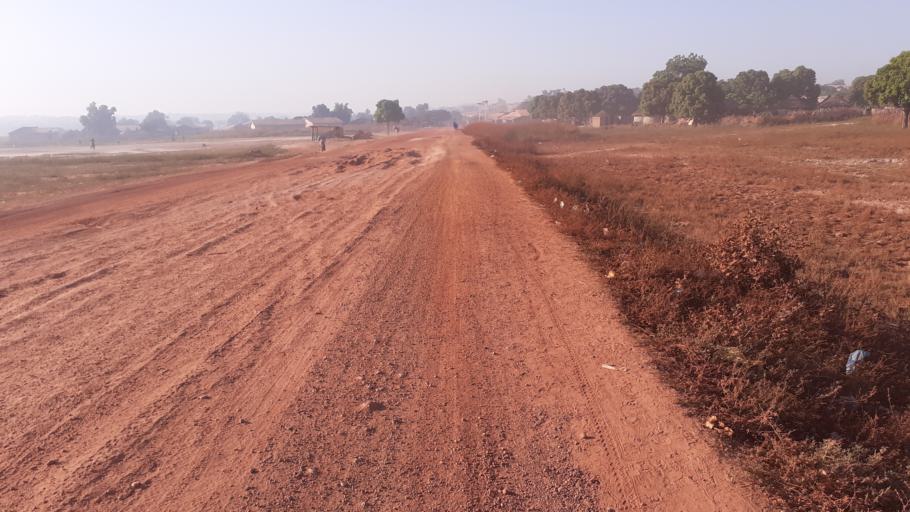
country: GN
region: Kankan
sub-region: Mandiana Prefecture
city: Mandiana
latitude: 10.9276
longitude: -8.8925
